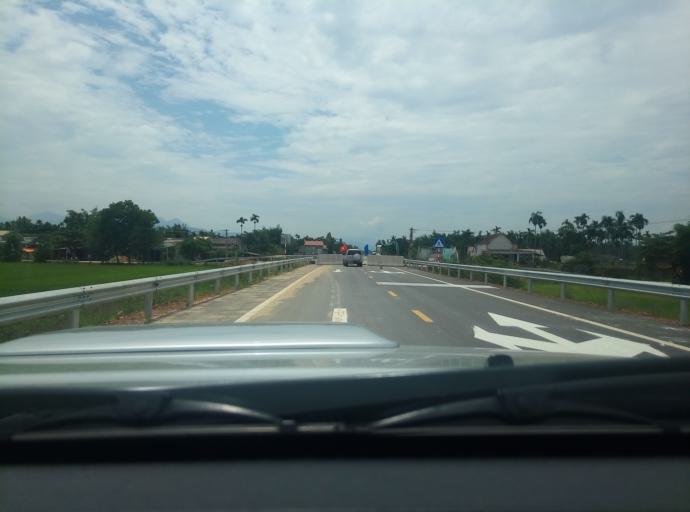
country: VN
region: Quang Ngai
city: Tu Nghia
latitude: 15.0723
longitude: 108.8140
